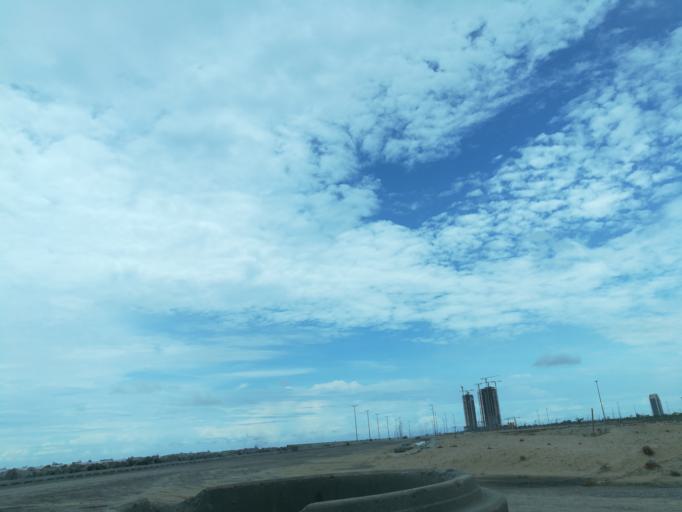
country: NG
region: Lagos
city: Ikoyi
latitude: 6.4073
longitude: 3.4227
